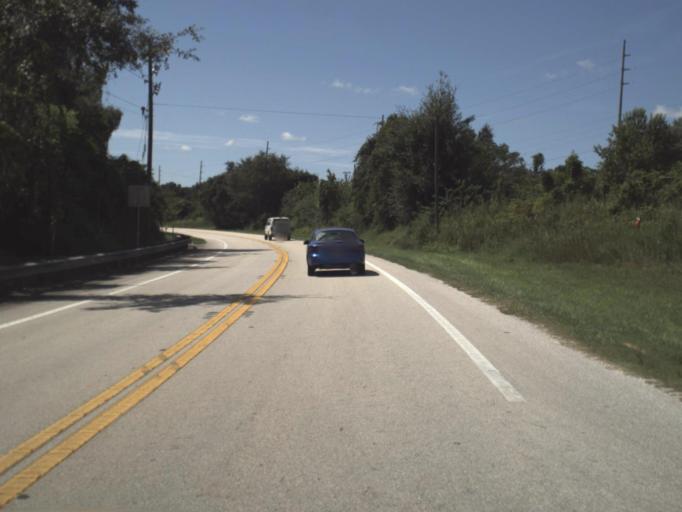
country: US
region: Florida
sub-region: Polk County
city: Lake Hamilton
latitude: 28.0469
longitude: -81.6205
